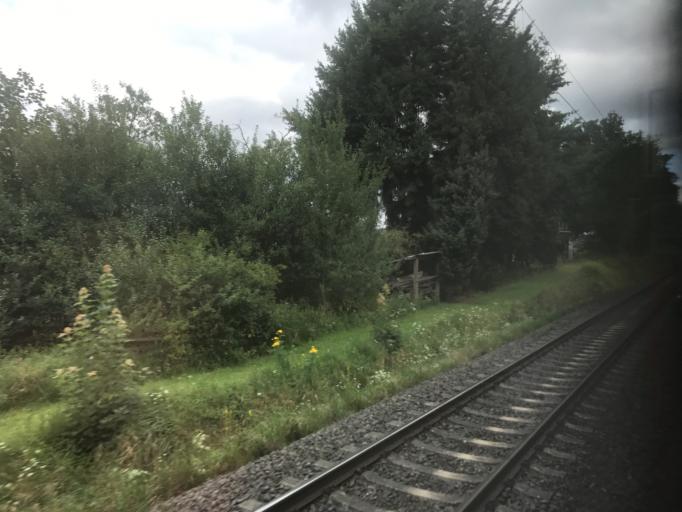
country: DE
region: Hesse
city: Schwalmstadt
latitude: 50.9364
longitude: 9.2038
